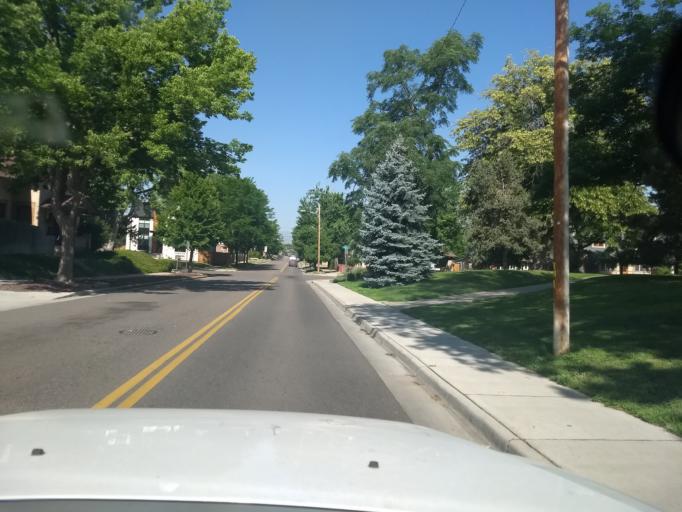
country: US
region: Colorado
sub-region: Arapahoe County
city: Englewood
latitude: 39.6876
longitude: -104.9833
